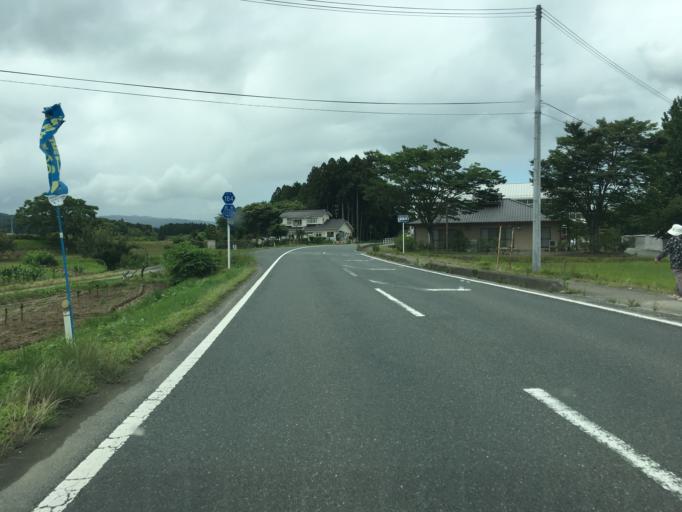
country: JP
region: Fukushima
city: Namie
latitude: 37.7249
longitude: 140.9305
